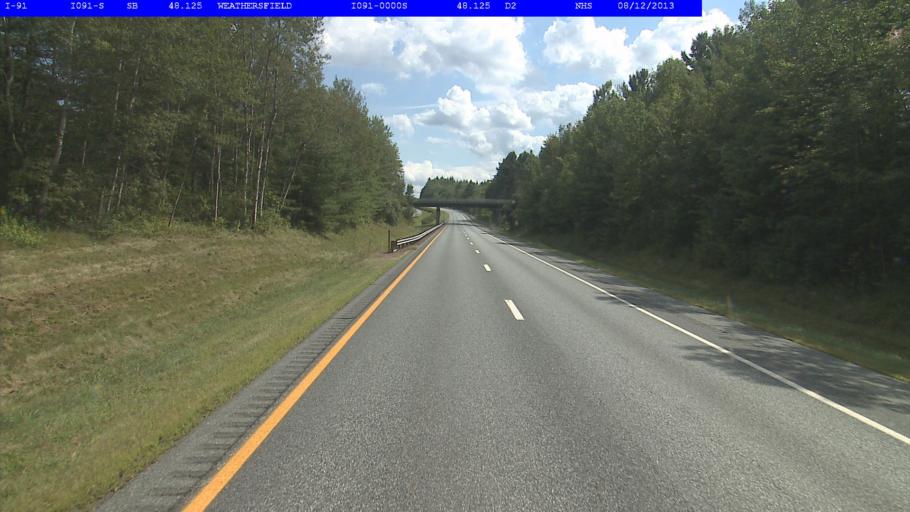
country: US
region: New Hampshire
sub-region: Sullivan County
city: Claremont
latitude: 43.3569
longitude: -72.4232
